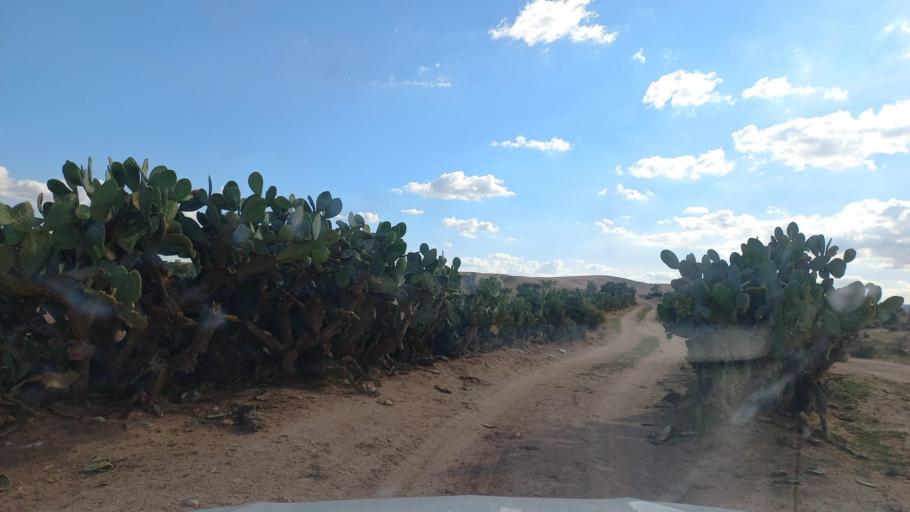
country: TN
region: Al Qasrayn
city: Sbiba
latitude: 35.3985
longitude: 9.0168
